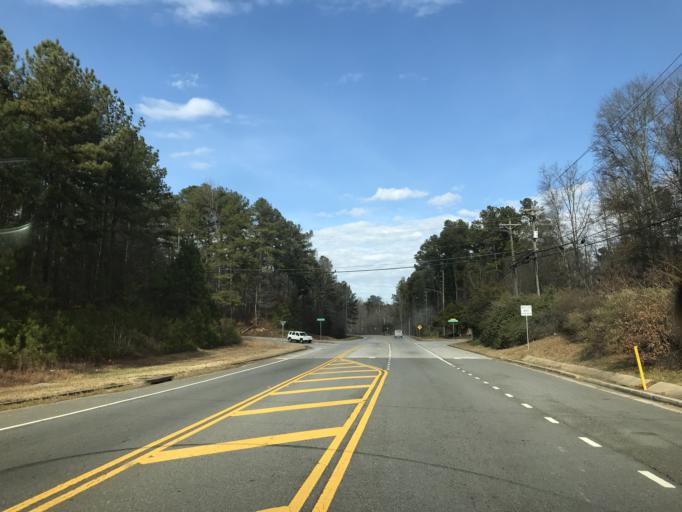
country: US
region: Georgia
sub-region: Douglas County
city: Douglasville
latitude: 33.7968
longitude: -84.8062
